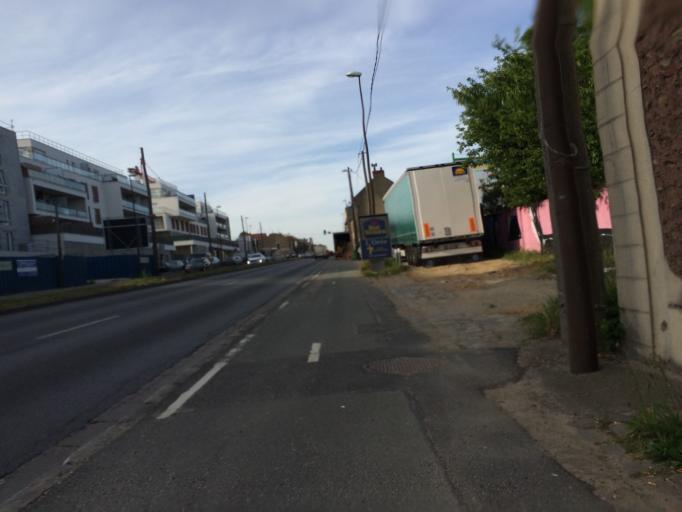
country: FR
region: Ile-de-France
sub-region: Departement de l'Essonne
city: La Ville-du-Bois
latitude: 48.6585
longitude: 2.2755
